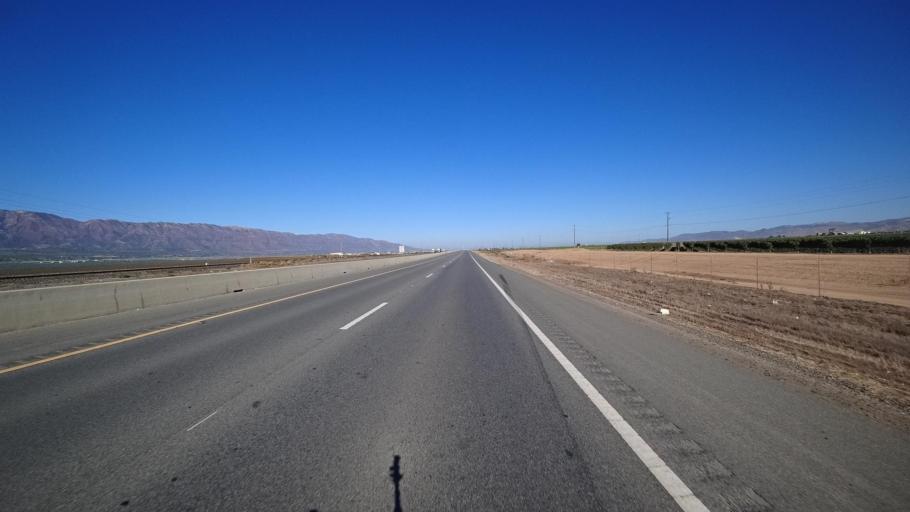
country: US
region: California
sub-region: Monterey County
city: Gonzales
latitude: 36.4709
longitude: -121.3962
